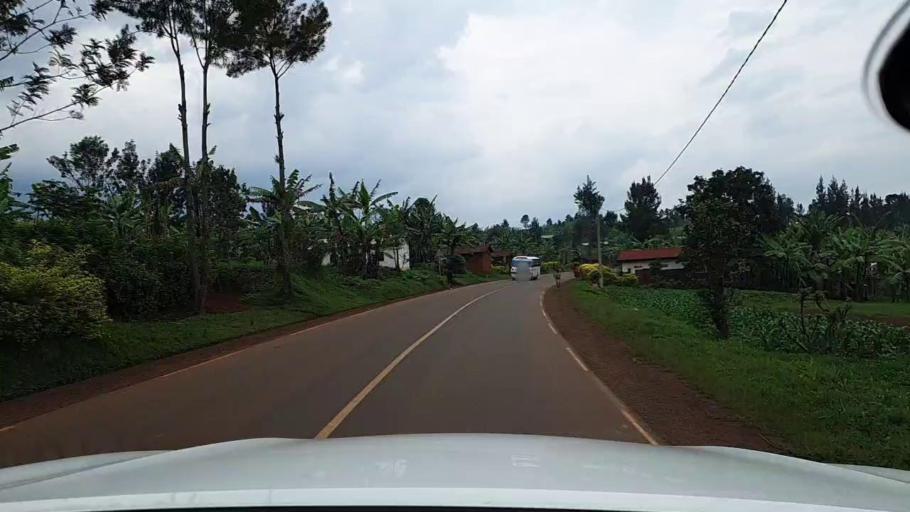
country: RW
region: Western Province
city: Cyangugu
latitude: -2.6141
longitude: 28.9429
